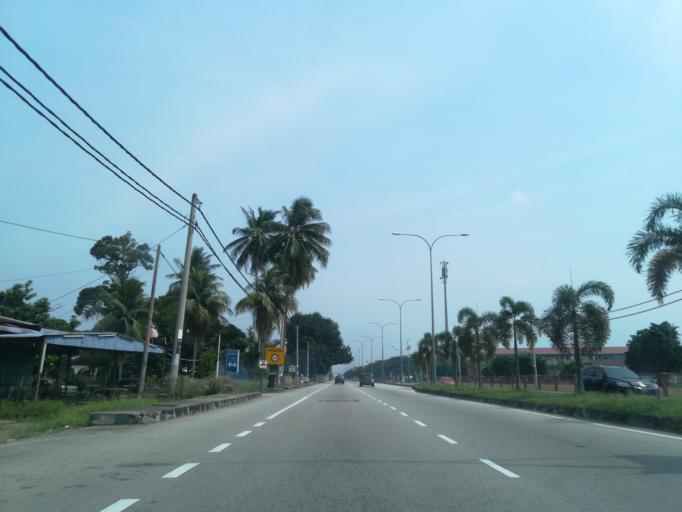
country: MY
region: Kedah
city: Kulim
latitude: 5.4000
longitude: 100.5567
